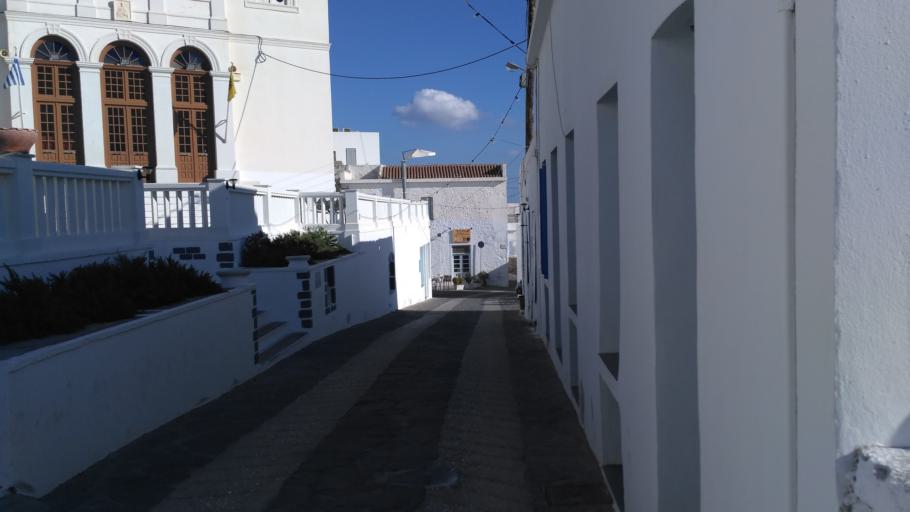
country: GR
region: South Aegean
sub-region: Nomos Kykladon
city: Milos
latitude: 36.7386
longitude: 24.4263
